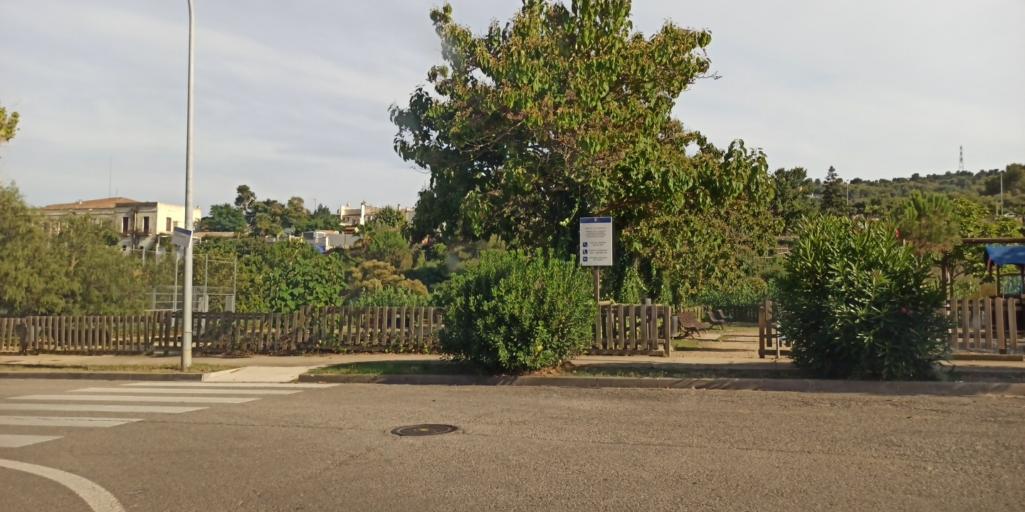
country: ES
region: Catalonia
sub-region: Provincia de Barcelona
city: Sant Boi de Llobregat
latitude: 41.3476
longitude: 2.0204
